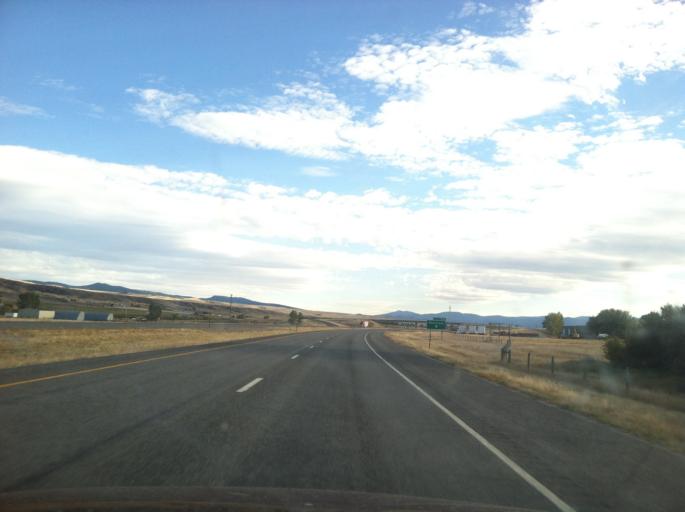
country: US
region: Montana
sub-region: Deer Lodge County
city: Warm Springs
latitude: 46.2759
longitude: -112.7474
